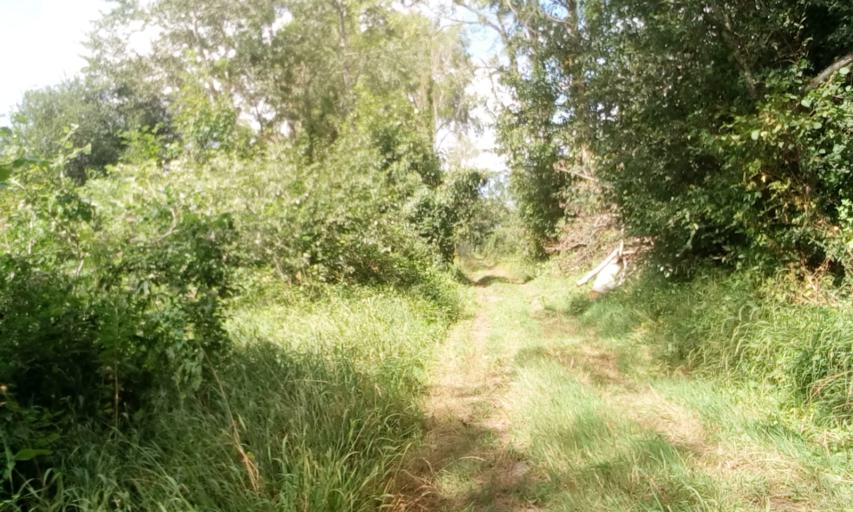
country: FR
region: Lower Normandy
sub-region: Departement du Calvados
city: Bellengreville
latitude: 49.1550
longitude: -0.2061
